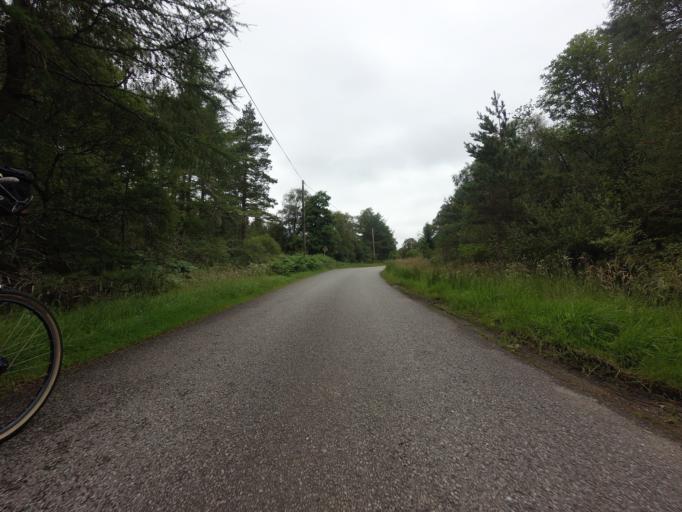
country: GB
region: Scotland
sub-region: Highland
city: Evanton
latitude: 57.9693
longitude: -4.4125
